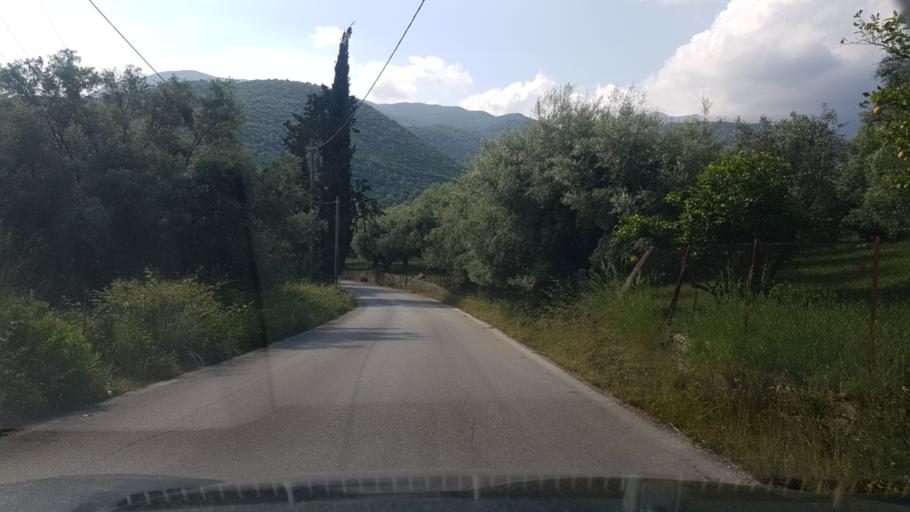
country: GR
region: Ionian Islands
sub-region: Lefkada
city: Nidri
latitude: 38.6551
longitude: 20.7014
